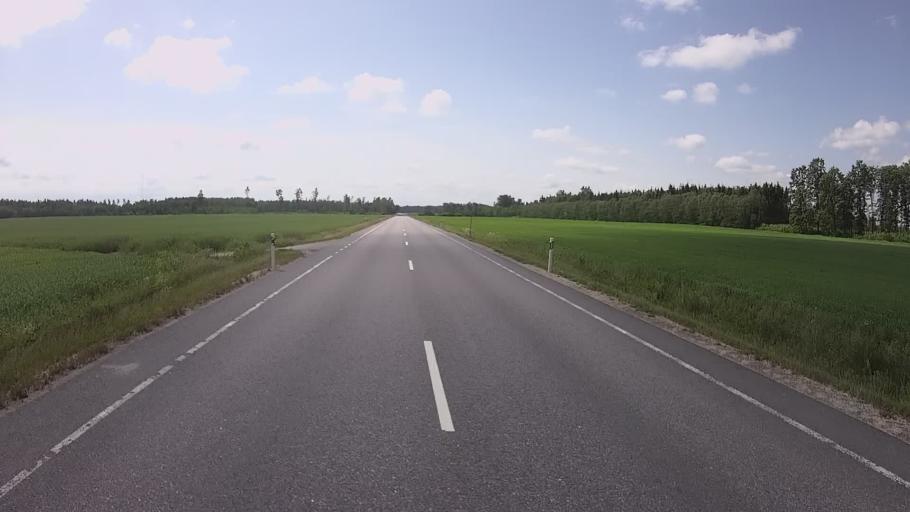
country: EE
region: Tartu
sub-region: Tartu linn
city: Tartu
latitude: 58.3887
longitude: 26.8903
